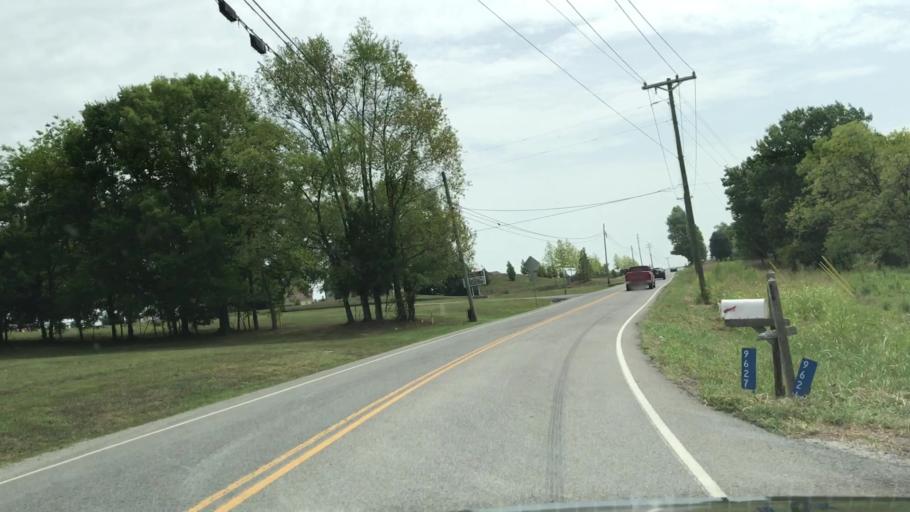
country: US
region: Tennessee
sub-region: Williamson County
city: Nolensville
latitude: 35.9379
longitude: -86.7083
